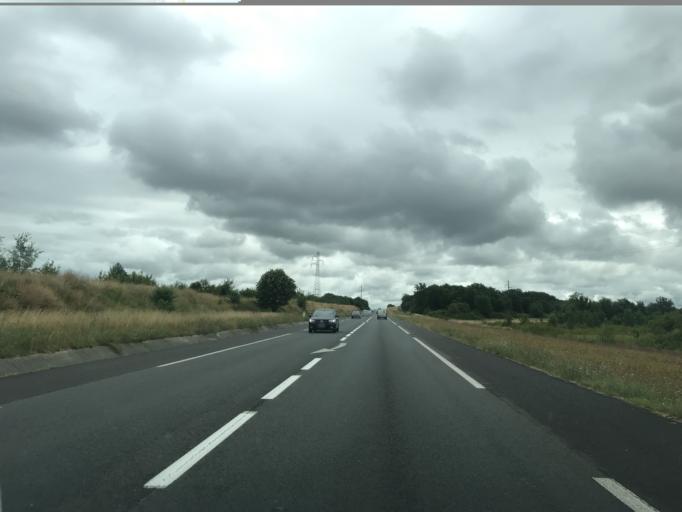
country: FR
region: Poitou-Charentes
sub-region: Departement de la Charente
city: Puymoyen
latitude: 45.6260
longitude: 0.1657
